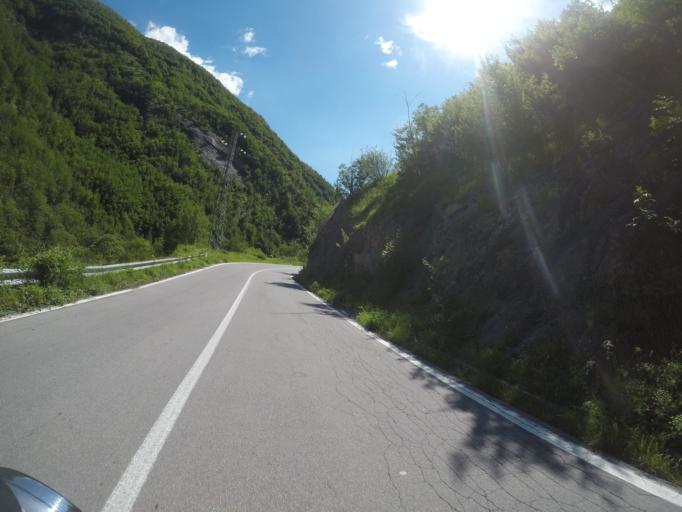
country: IT
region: Tuscany
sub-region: Provincia di Lucca
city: Fontana delle Monache
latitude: 44.0620
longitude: 10.2923
